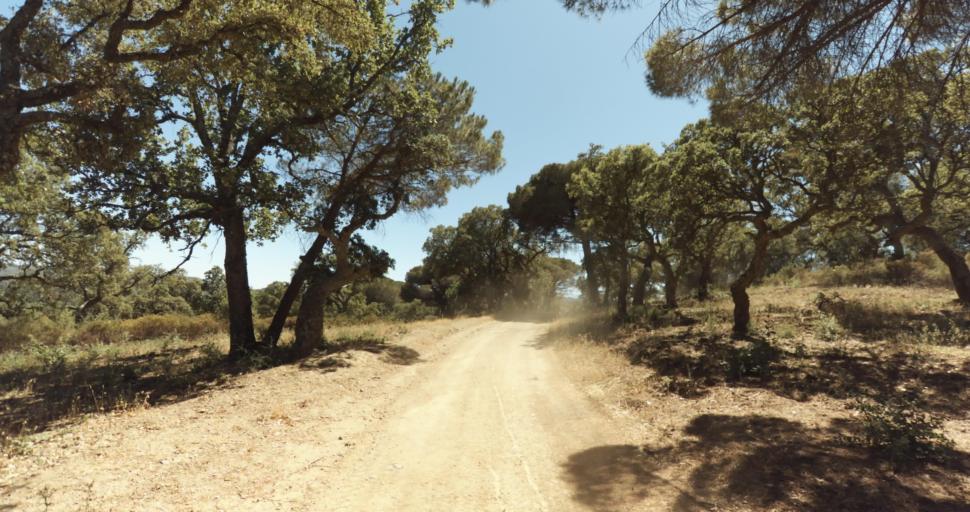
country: FR
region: Provence-Alpes-Cote d'Azur
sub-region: Departement du Var
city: Gassin
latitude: 43.2501
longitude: 6.5639
